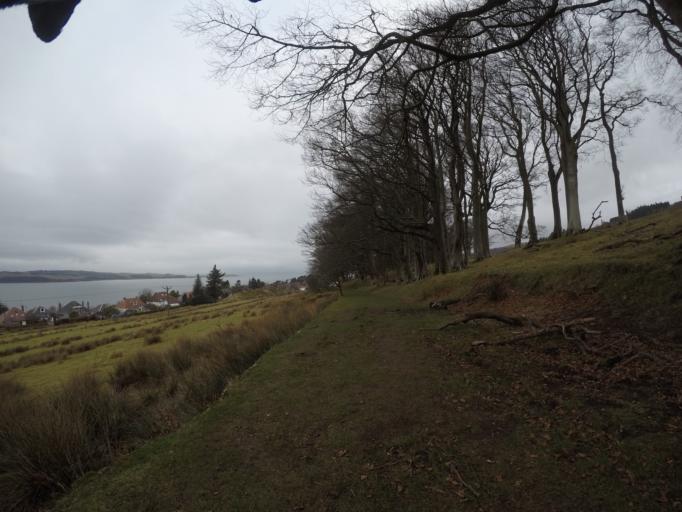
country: GB
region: Scotland
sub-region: North Ayrshire
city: Fairlie
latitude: 55.7555
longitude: -4.8492
